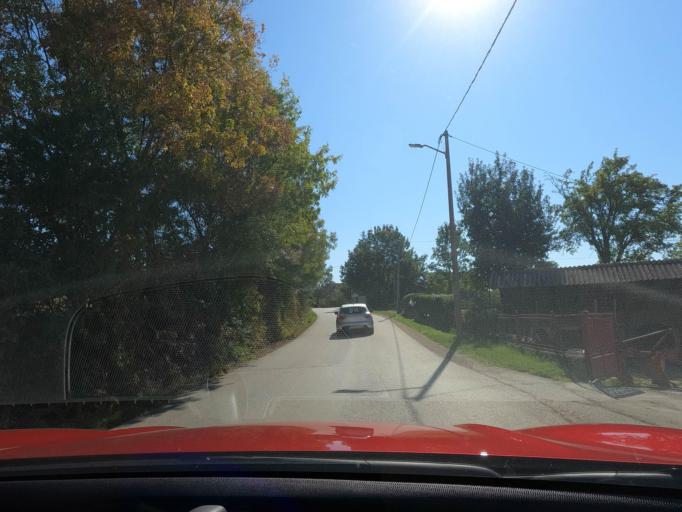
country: RS
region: Central Serbia
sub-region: Raski Okrug
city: Kraljevo
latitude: 43.7643
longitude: 20.6734
